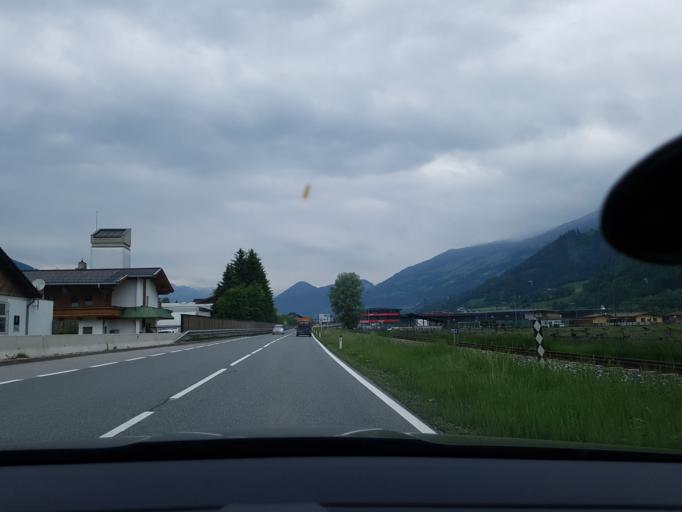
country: AT
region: Tyrol
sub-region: Politischer Bezirk Schwaz
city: Uderns
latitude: 47.3185
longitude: 11.8653
